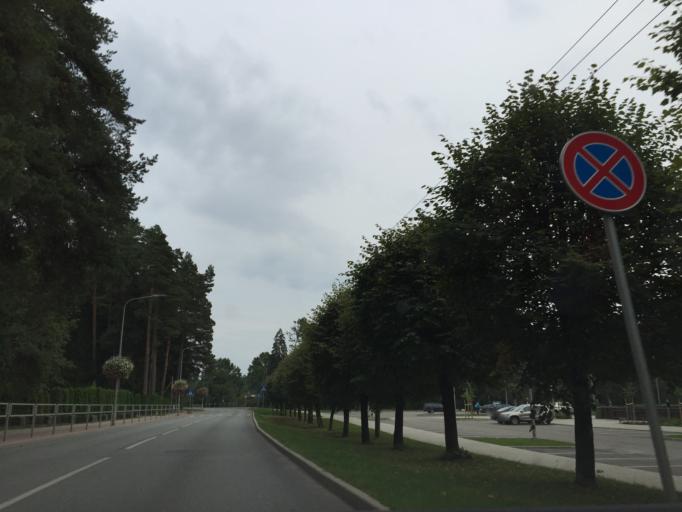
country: LV
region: Ogre
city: Ogre
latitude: 56.8176
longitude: 24.6177
